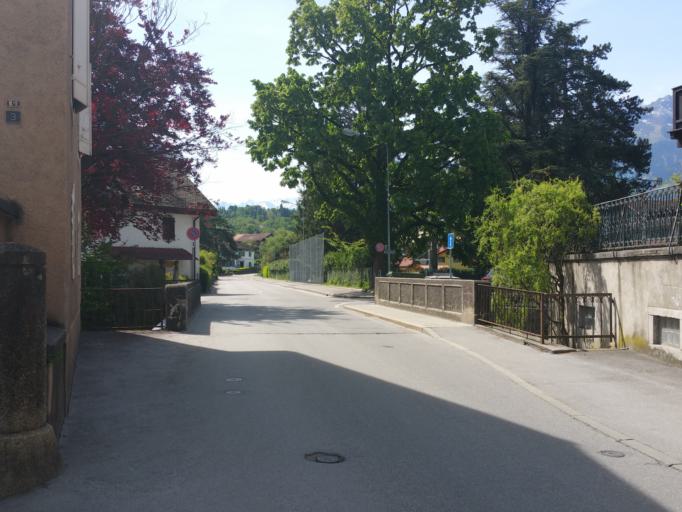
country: CH
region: Vaud
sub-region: Aigle District
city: Bex
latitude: 46.2492
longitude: 7.0124
